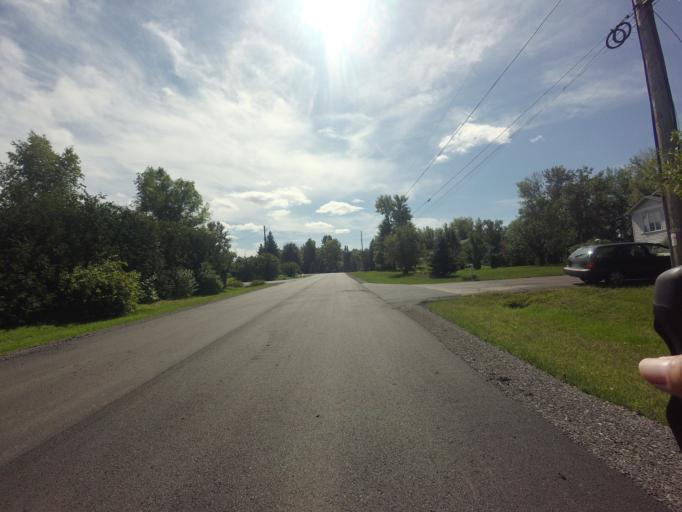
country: CA
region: Ontario
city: Carleton Place
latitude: 45.1350
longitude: -76.0666
